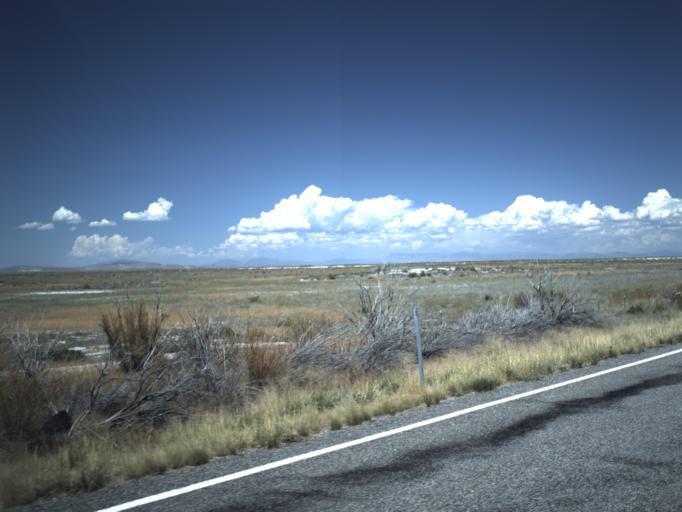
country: US
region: Utah
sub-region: Millard County
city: Delta
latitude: 39.2698
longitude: -112.8640
